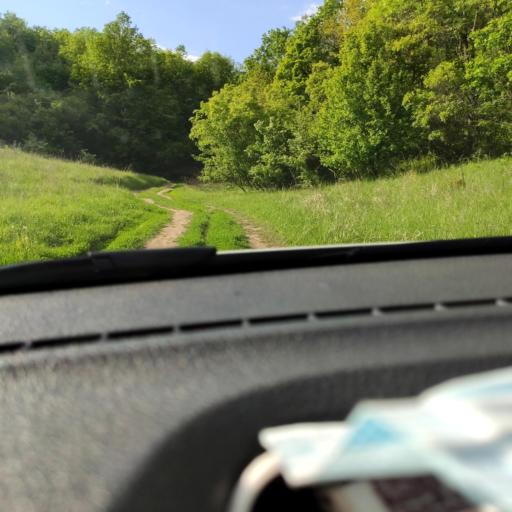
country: RU
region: Voronezj
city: Ramon'
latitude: 51.9403
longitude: 39.3694
